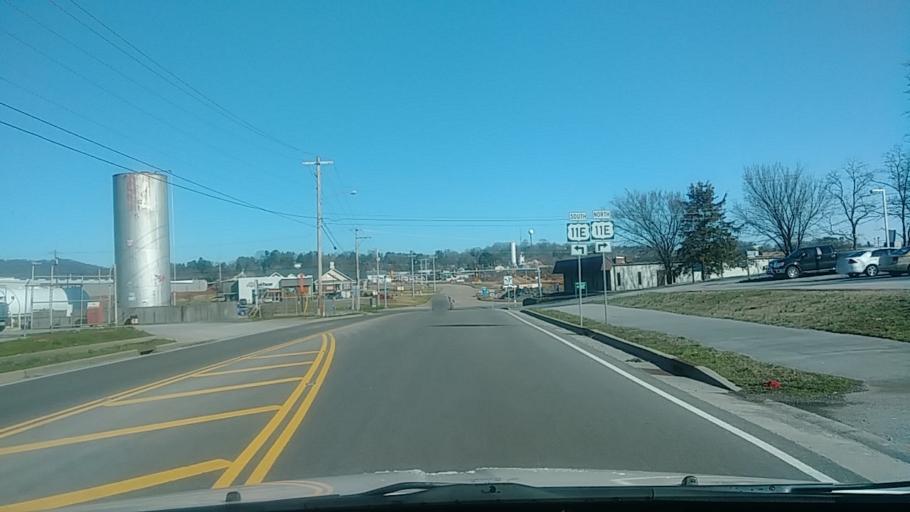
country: US
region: Tennessee
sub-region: Hamblen County
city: Morristown
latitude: 36.2016
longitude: -83.3107
